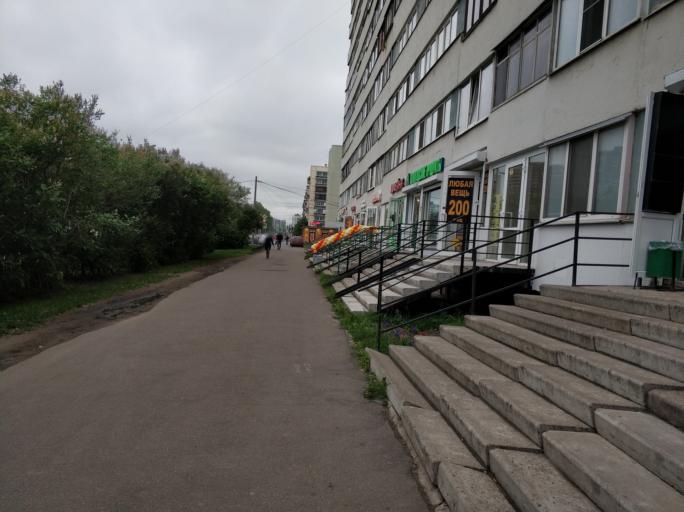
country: RU
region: St.-Petersburg
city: Grazhdanka
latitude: 60.0360
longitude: 30.4106
